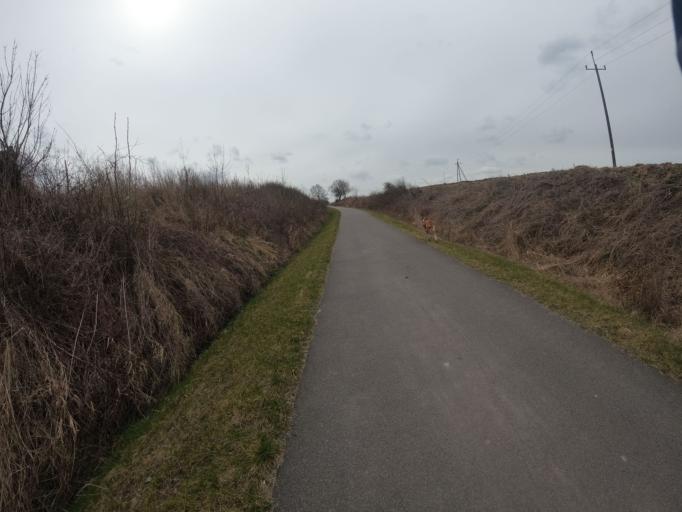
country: PL
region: West Pomeranian Voivodeship
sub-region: Powiat gryficki
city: Trzebiatow
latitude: 54.0889
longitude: 15.2684
